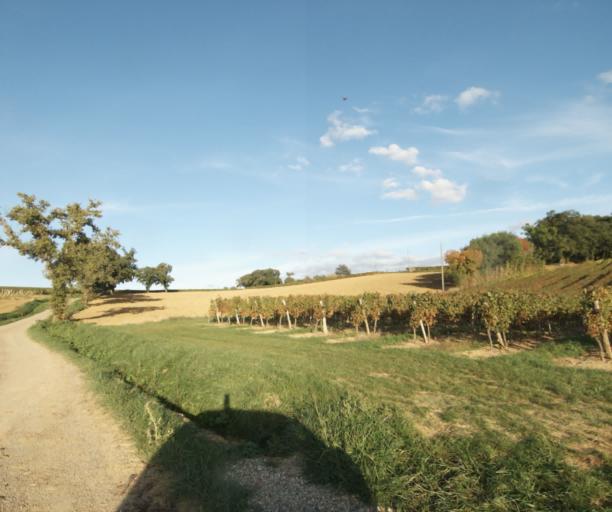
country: FR
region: Midi-Pyrenees
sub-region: Departement du Gers
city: Valence-sur-Baise
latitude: 43.8742
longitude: 0.3103
